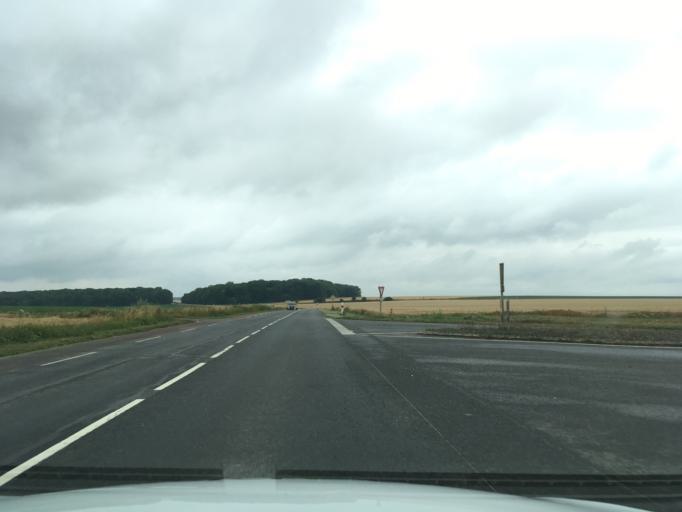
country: FR
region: Picardie
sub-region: Departement de la Somme
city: Doingt
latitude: 49.8911
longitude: 3.0312
